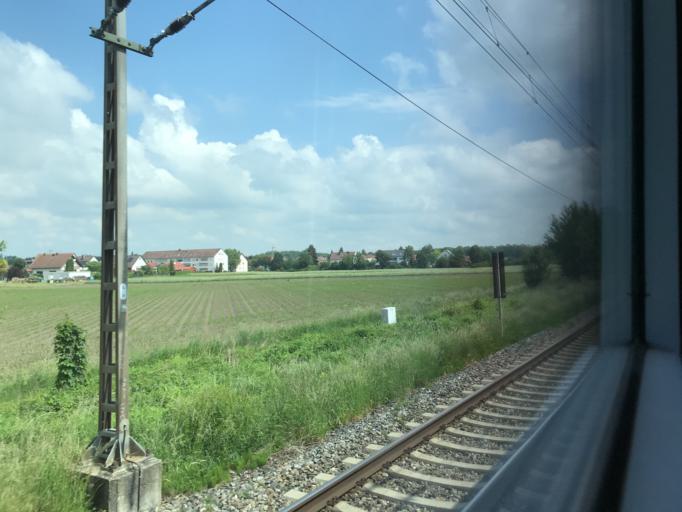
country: DE
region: Bavaria
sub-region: Swabia
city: Nersingen
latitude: 48.4271
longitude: 10.1106
